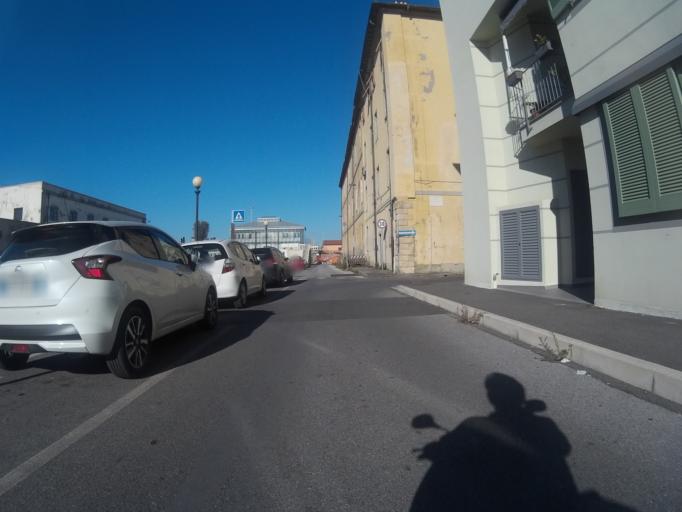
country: IT
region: Tuscany
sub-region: Provincia di Livorno
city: Livorno
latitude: 43.5580
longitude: 10.3109
